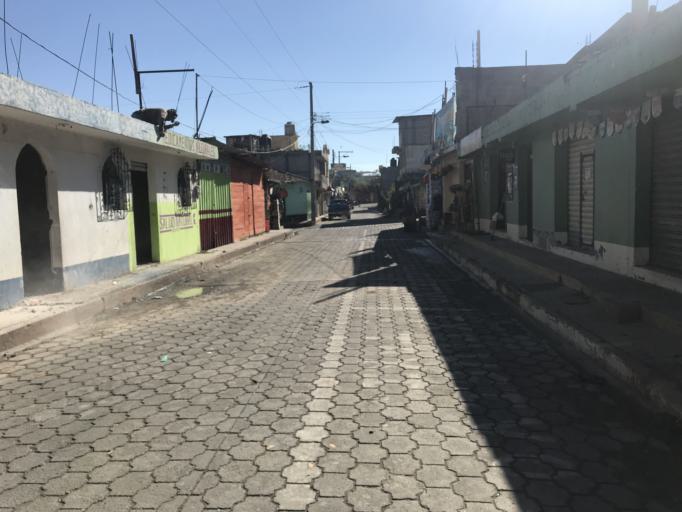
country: GT
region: San Marcos
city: San Miguel Ixtahuacan
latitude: 15.2719
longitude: -91.7482
